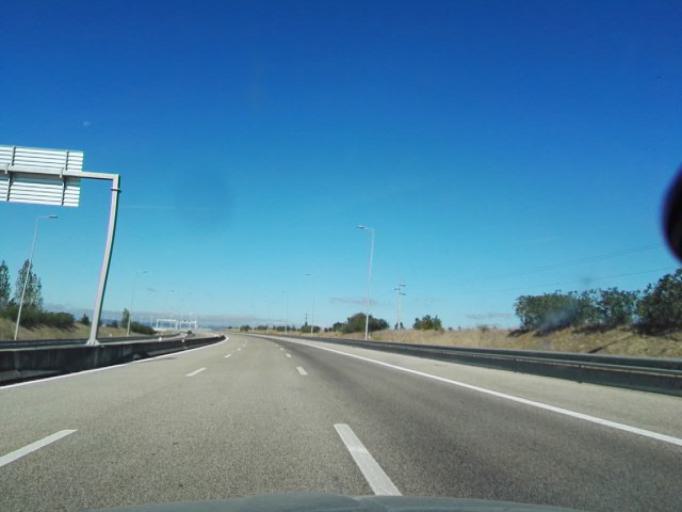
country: PT
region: Santarem
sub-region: Benavente
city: Benavente
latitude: 38.9655
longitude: -8.8401
